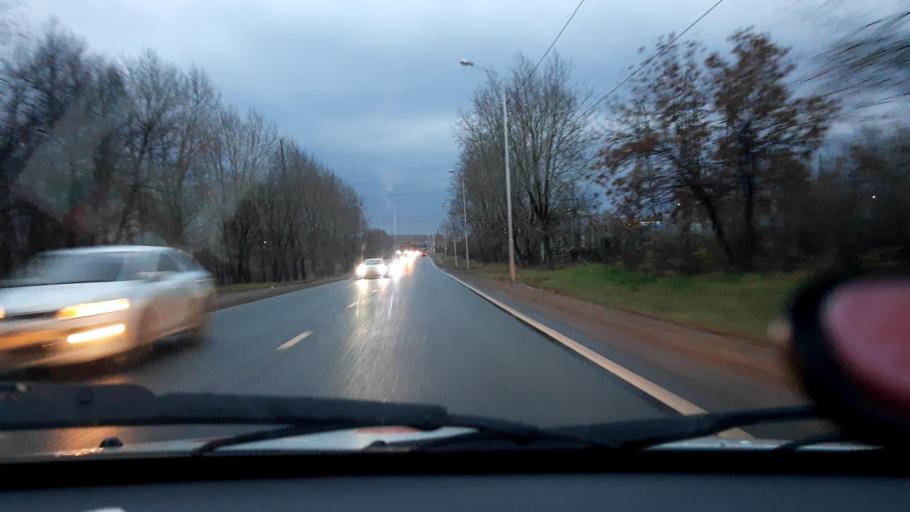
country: RU
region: Bashkortostan
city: Ufa
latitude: 54.8536
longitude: 56.1162
